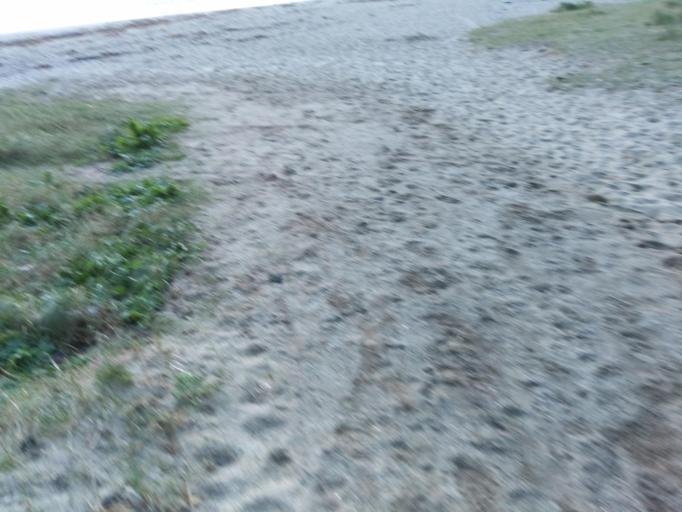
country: GB
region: England
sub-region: Cornwall
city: Fowey
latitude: 50.3286
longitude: -4.6029
